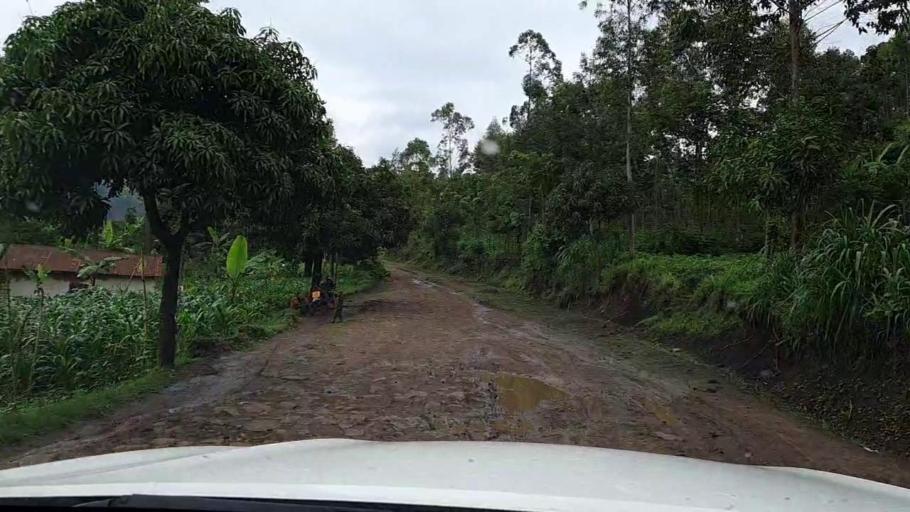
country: RW
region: Western Province
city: Cyangugu
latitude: -2.5492
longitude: 29.0384
